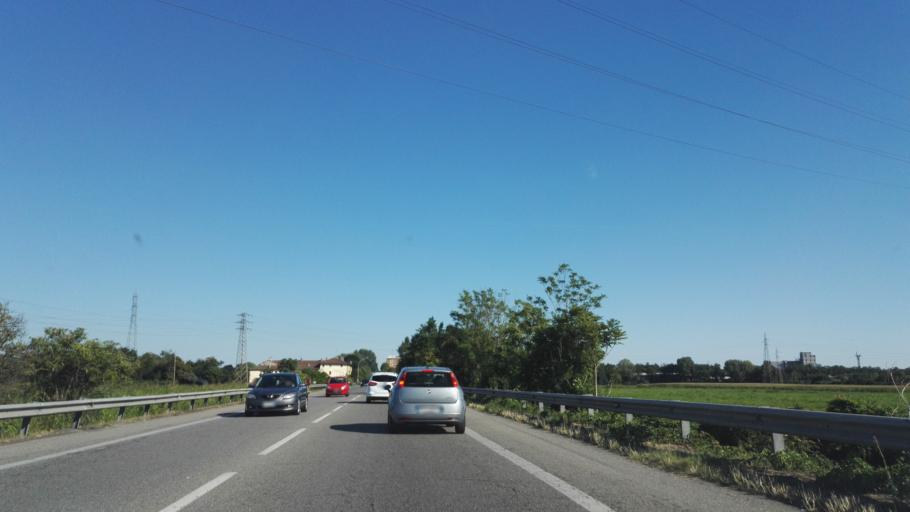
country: IT
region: Lombardy
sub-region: Citta metropolitana di Milano
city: Melegnano
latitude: 45.3708
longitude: 9.3129
